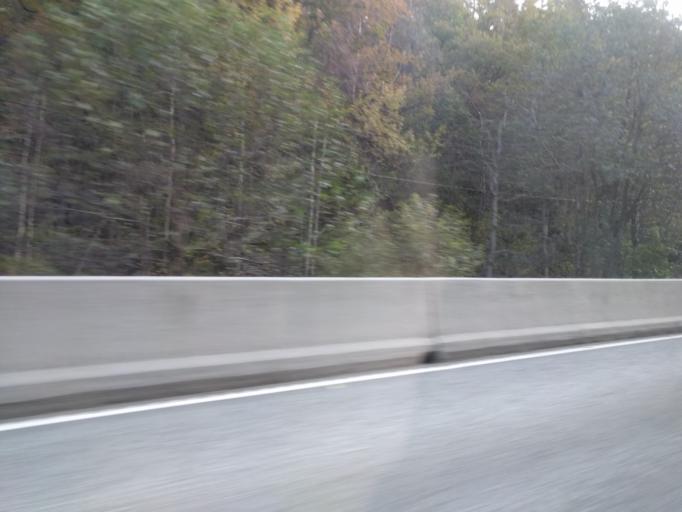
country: NO
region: Vest-Agder
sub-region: Kristiansand
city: Strai
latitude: 58.2454
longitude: 7.8752
